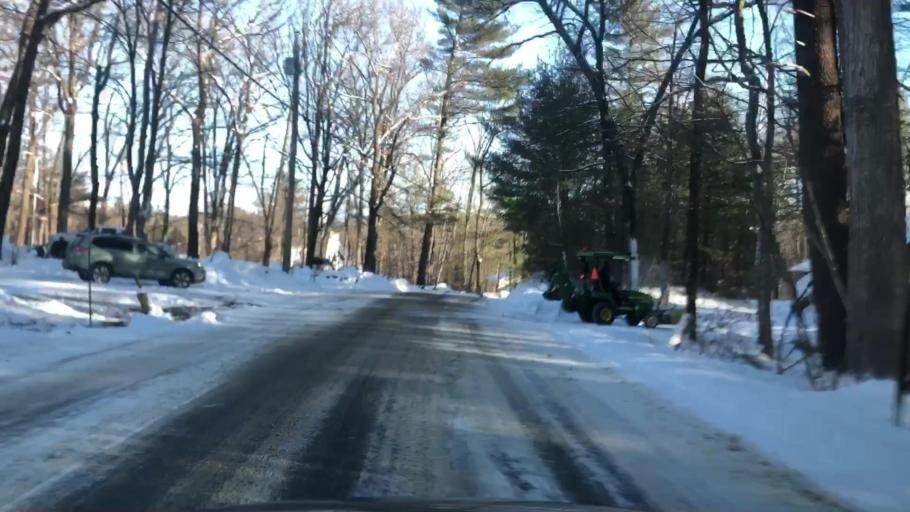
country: US
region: New Hampshire
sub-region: Hillsborough County
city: Wilton
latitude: 42.8126
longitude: -71.7137
